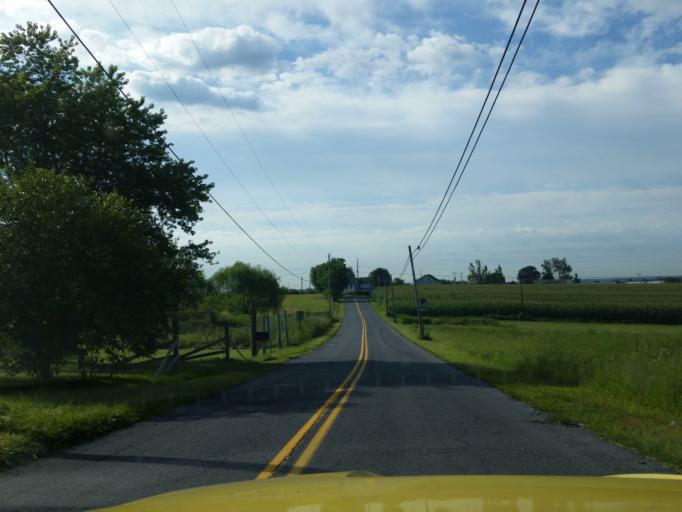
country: US
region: Pennsylvania
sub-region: Lebanon County
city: Fredericksburg
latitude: 40.4565
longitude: -76.4358
